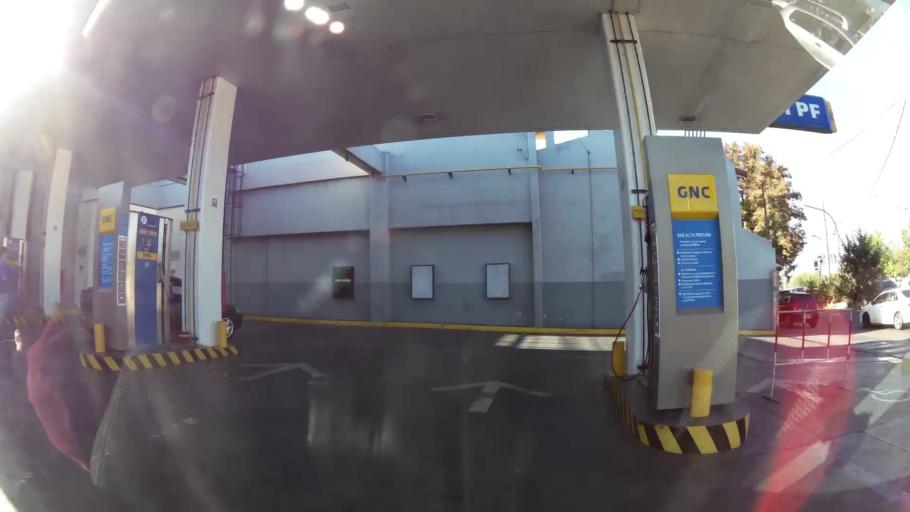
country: AR
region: Mendoza
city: Mendoza
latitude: -32.8994
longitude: -68.8358
